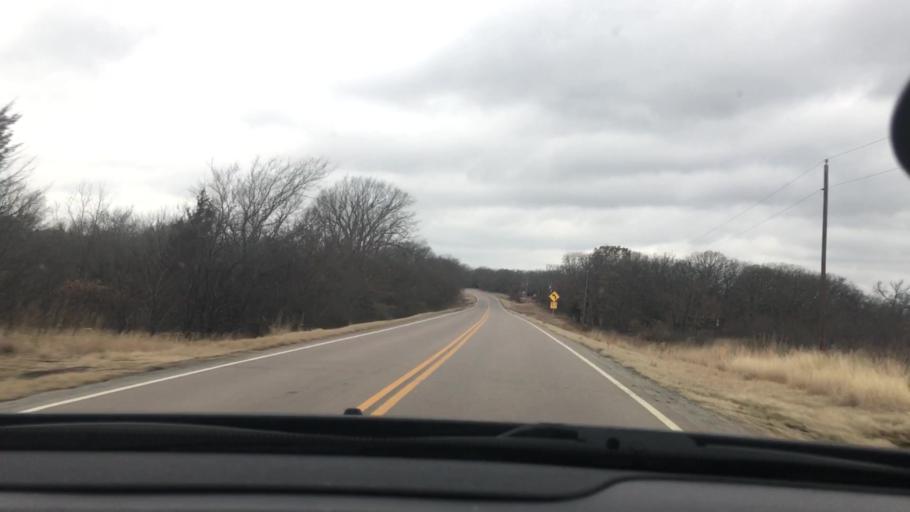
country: US
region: Oklahoma
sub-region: Coal County
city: Coalgate
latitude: 34.3743
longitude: -96.3664
